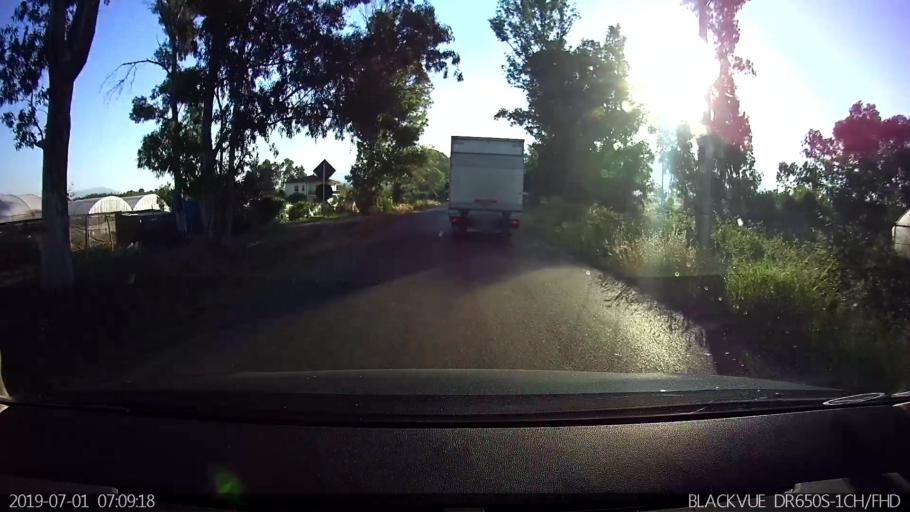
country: IT
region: Latium
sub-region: Provincia di Latina
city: Borgo Hermada
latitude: 41.3043
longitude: 13.1596
